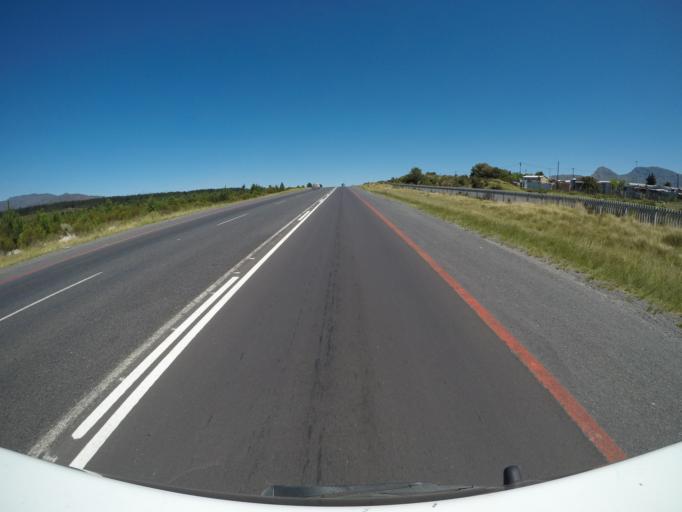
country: ZA
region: Western Cape
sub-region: Overberg District Municipality
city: Grabouw
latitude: -34.1660
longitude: 18.9962
